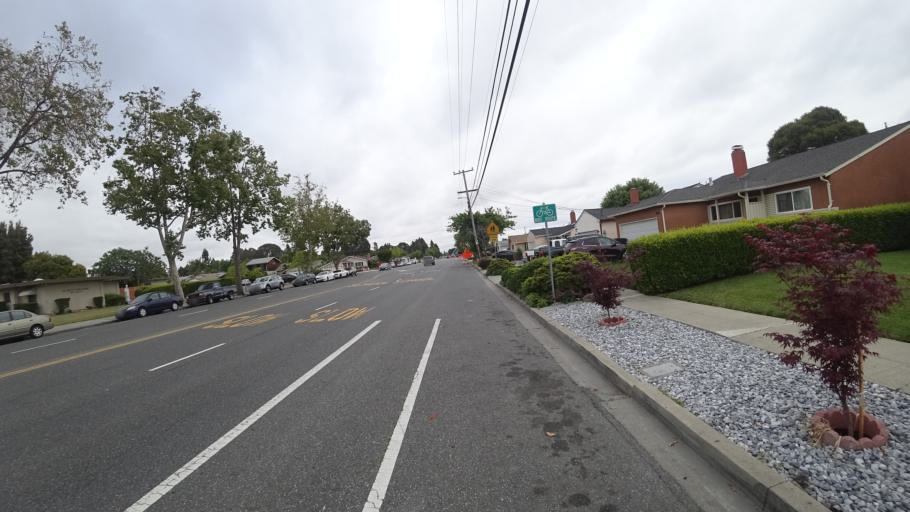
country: US
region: California
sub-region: Alameda County
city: Hayward
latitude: 37.6381
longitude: -122.0798
